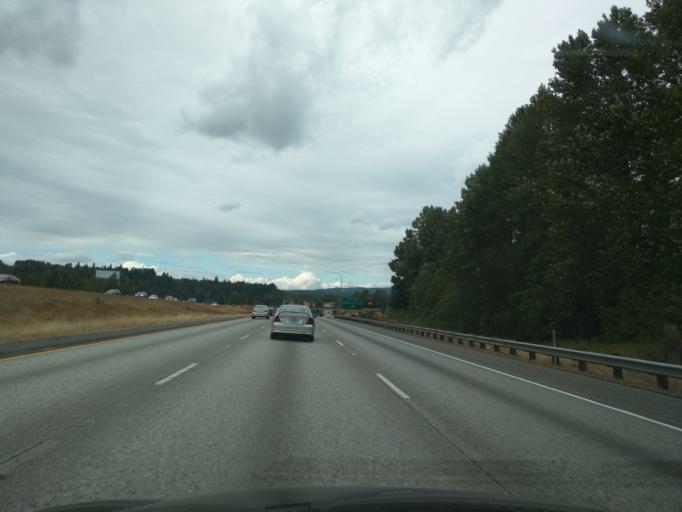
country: US
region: Washington
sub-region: Snohomish County
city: Smokey Point
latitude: 48.2052
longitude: -122.2137
